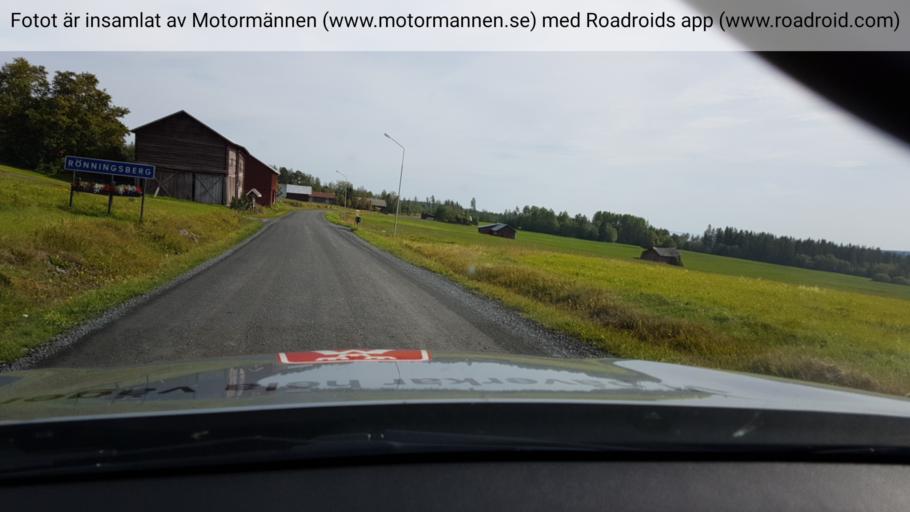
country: SE
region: Jaemtland
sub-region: Krokoms Kommun
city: Valla
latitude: 63.3520
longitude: 13.9837
